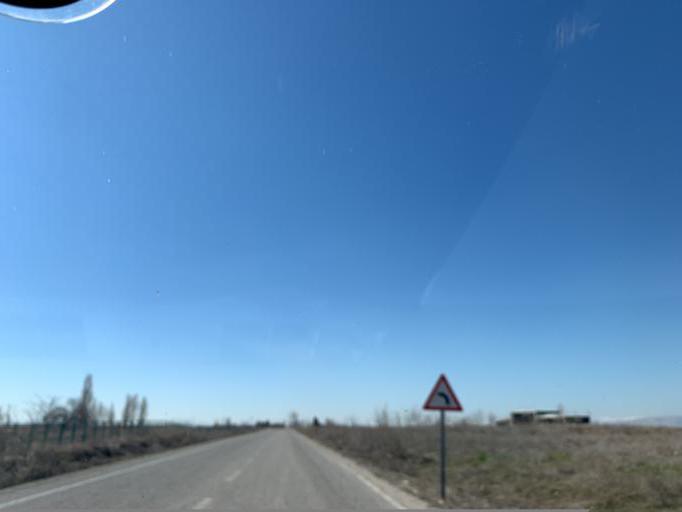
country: TR
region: Konya
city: Cumra
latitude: 37.6151
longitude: 32.7973
